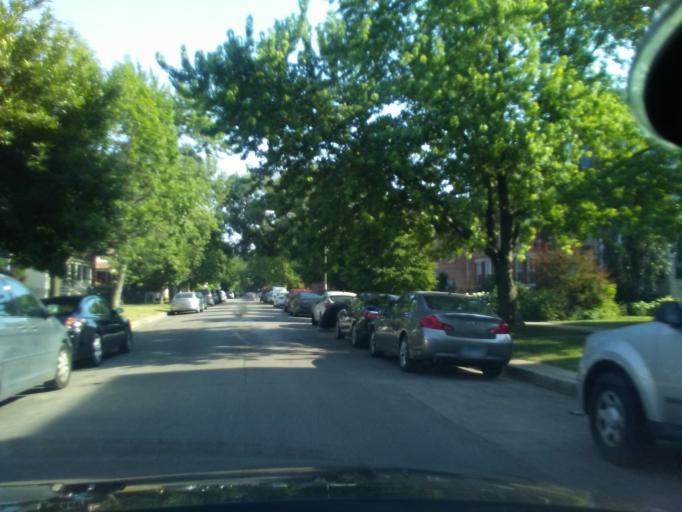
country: US
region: Illinois
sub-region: Cook County
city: Lincolnwood
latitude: 41.9700
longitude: -87.6711
